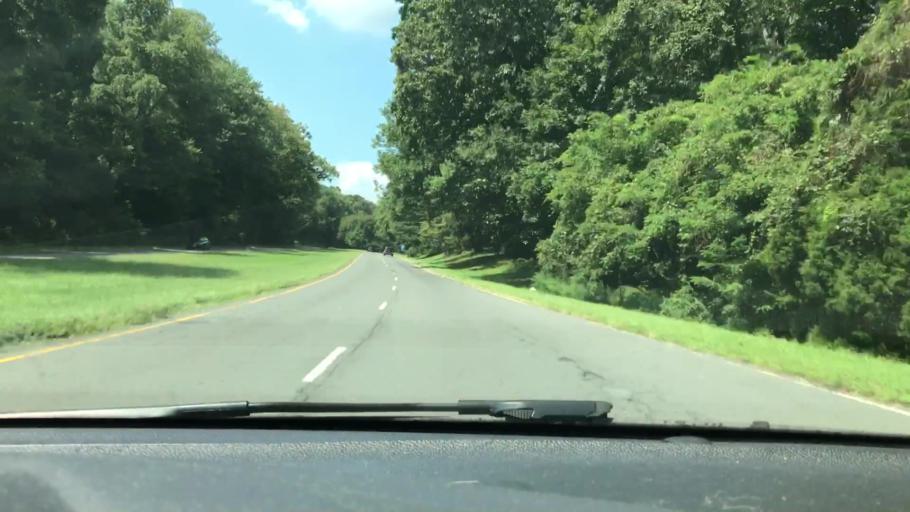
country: US
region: Maryland
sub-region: Montgomery County
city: Brookmont
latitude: 38.9413
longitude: -77.1339
